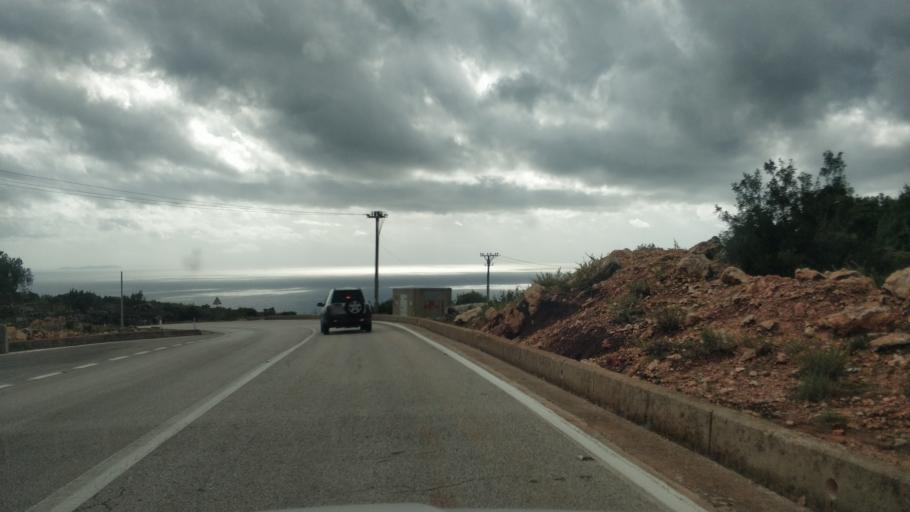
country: AL
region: Vlore
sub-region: Rrethi i Vlores
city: Vranisht
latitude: 40.1440
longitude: 19.6527
